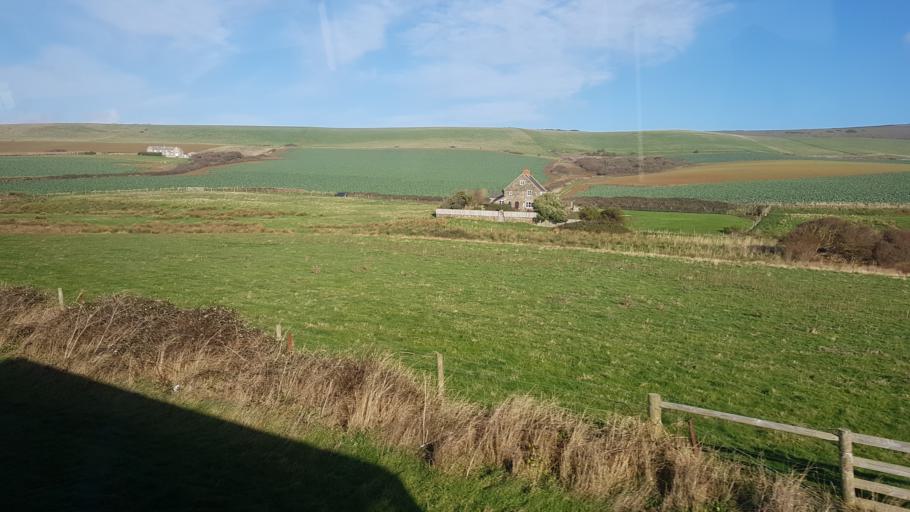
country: GB
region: England
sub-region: Isle of Wight
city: Freshwater
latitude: 50.6541
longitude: -1.4643
